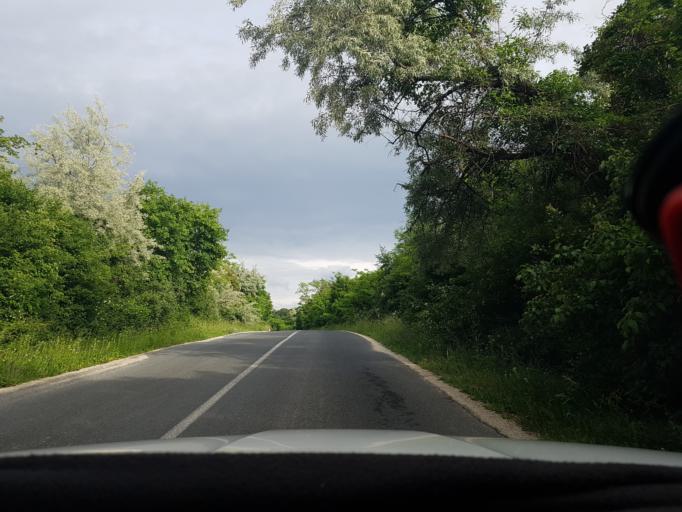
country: HU
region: Komarom-Esztergom
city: Nyergesujfalu
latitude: 47.7270
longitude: 18.5351
